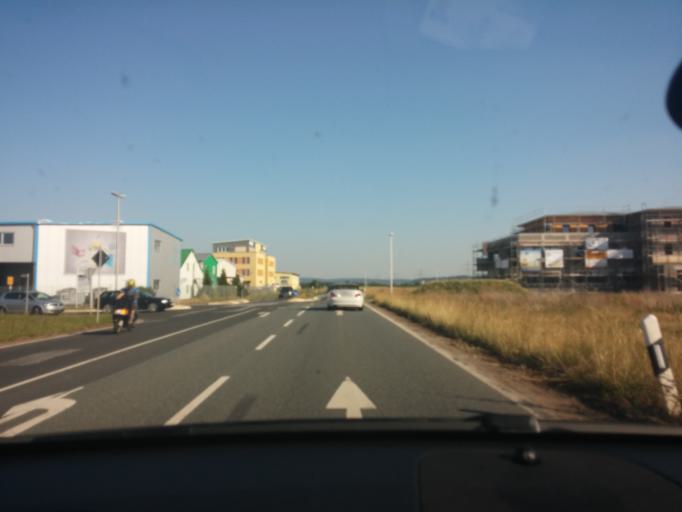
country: DE
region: Bavaria
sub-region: Regierungsbezirk Unterfranken
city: Niedernberg
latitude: 49.9126
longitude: 9.1255
